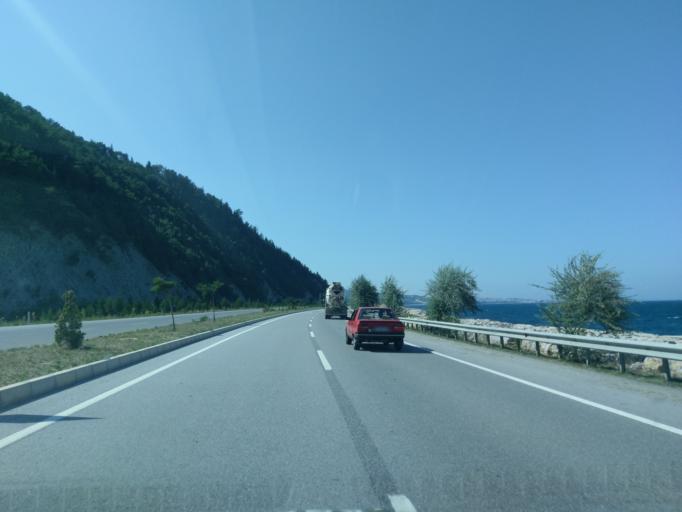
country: TR
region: Sinop
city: Gerze
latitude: 41.7471
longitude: 35.2442
